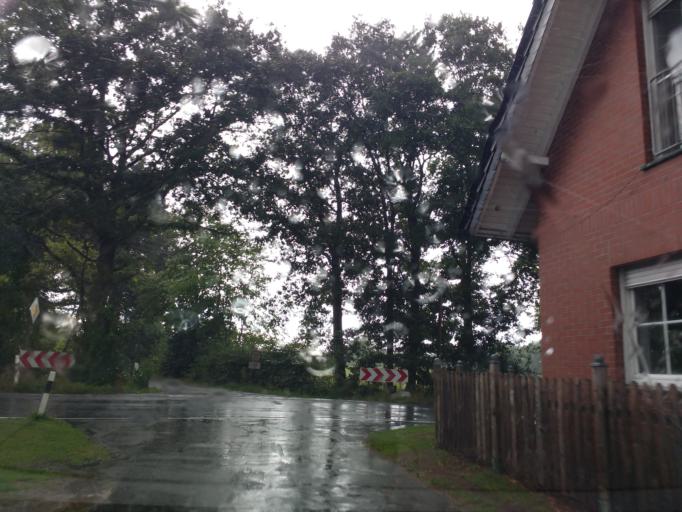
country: DE
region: North Rhine-Westphalia
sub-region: Regierungsbezirk Munster
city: Ostbevern
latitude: 52.1113
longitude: 7.8889
